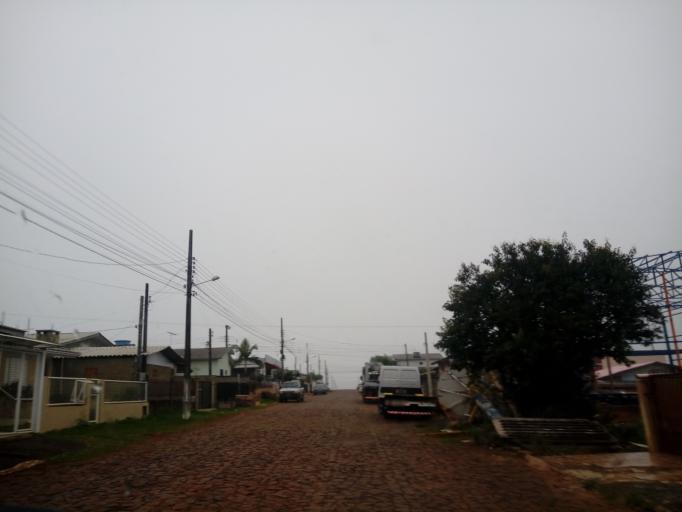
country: BR
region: Santa Catarina
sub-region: Chapeco
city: Chapeco
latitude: -27.1073
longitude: -52.6749
